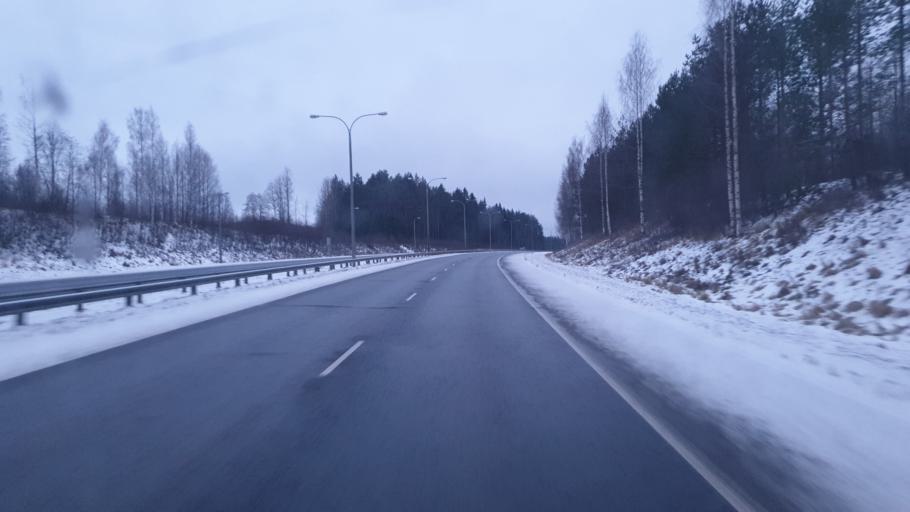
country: FI
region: Northern Savo
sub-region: Kuopio
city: Siilinjaervi
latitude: 63.0562
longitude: 27.6712
